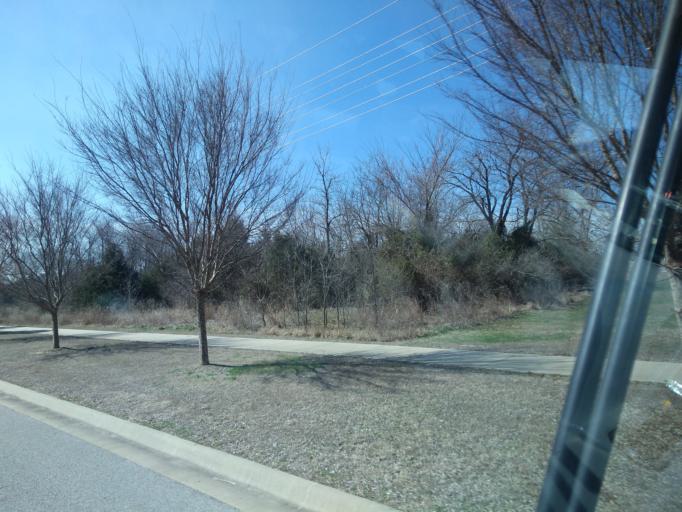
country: US
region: Arkansas
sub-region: Washington County
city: Farmington
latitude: 36.0628
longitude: -94.2313
